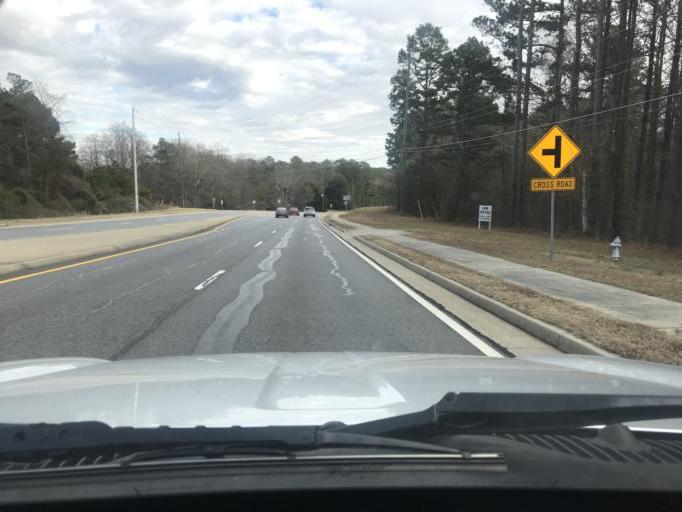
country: US
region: Georgia
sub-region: Gwinnett County
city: Buford
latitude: 34.0741
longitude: -83.9799
